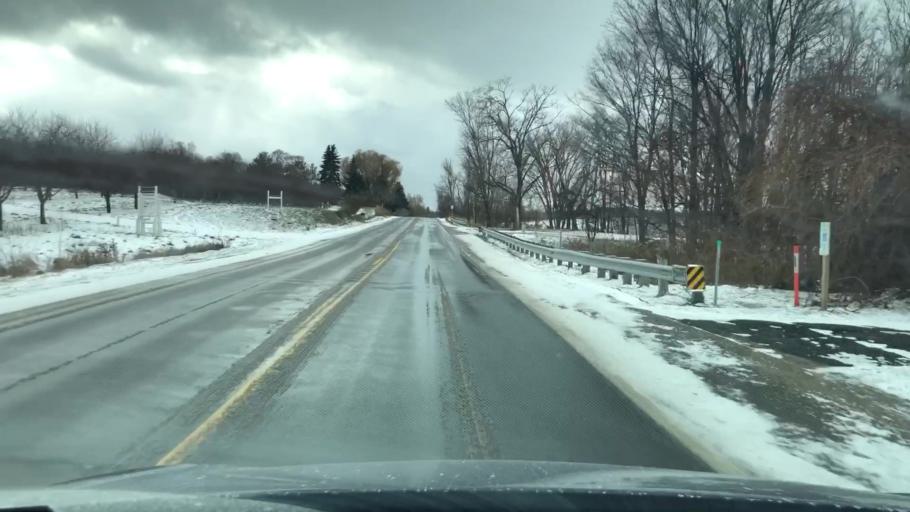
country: US
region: Michigan
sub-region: Antrim County
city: Elk Rapids
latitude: 44.8802
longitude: -85.5154
